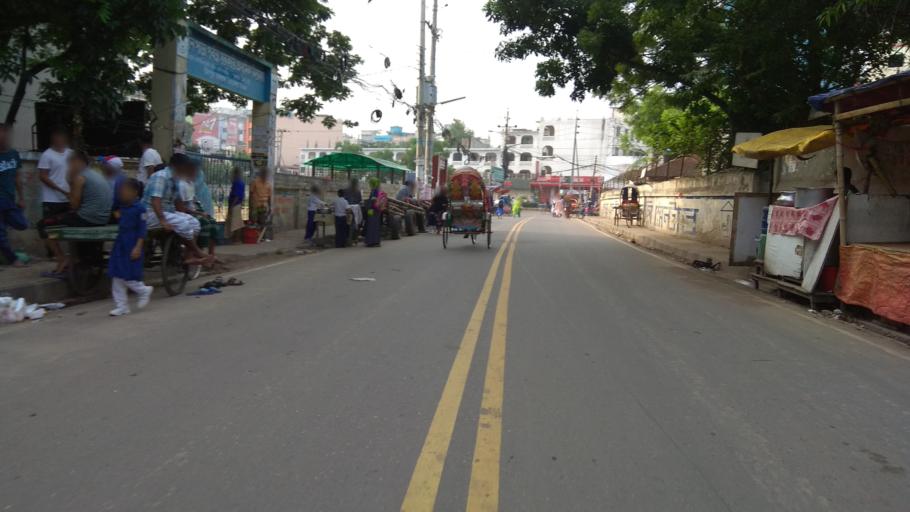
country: BD
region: Dhaka
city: Azimpur
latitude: 23.8079
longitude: 90.3700
